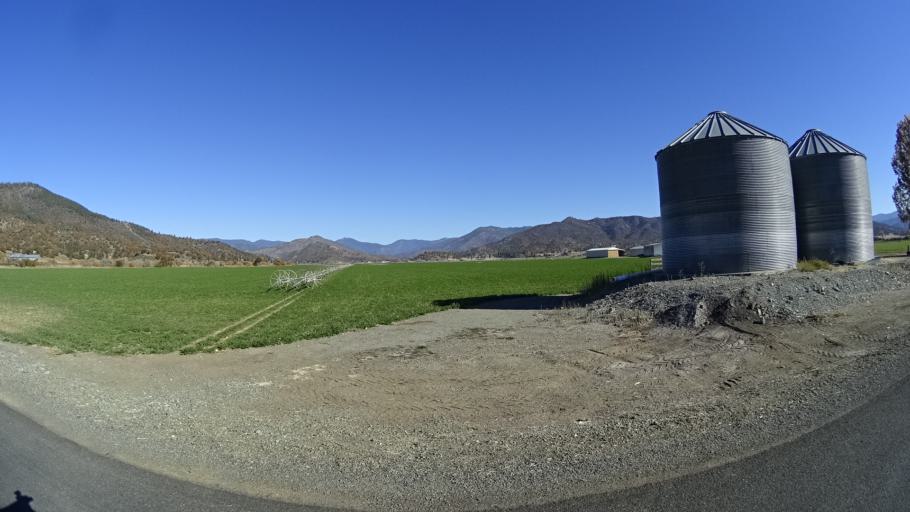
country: US
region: California
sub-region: Siskiyou County
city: Yreka
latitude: 41.5749
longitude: -122.8559
